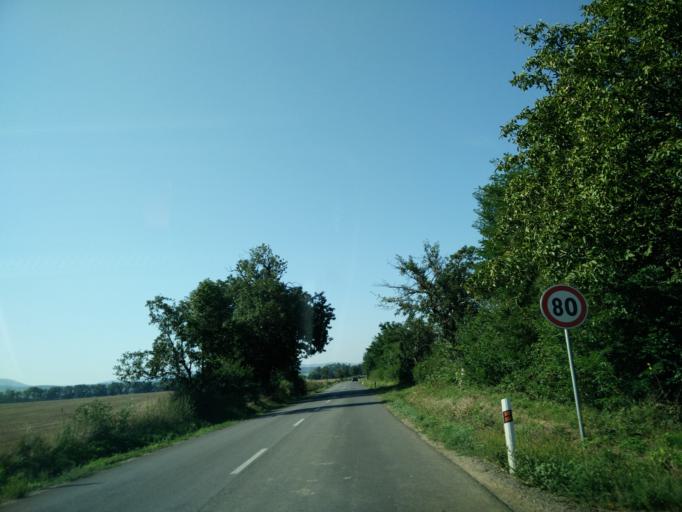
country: SK
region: Nitriansky
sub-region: Okres Nitra
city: Nitra
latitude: 48.4448
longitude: 18.1406
